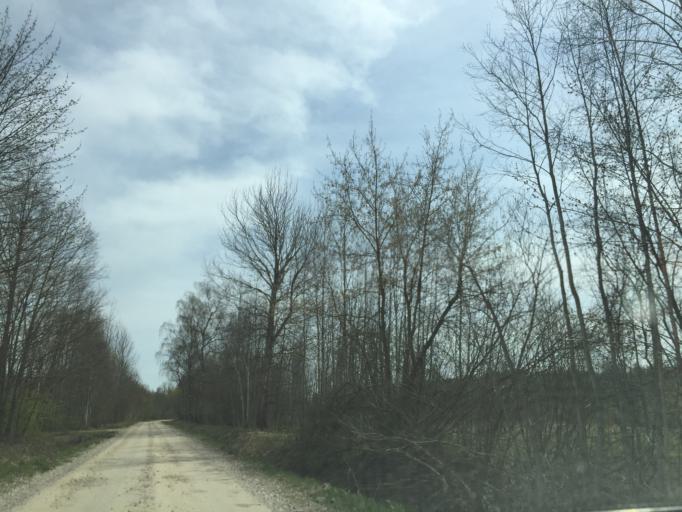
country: LV
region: Ludzas Rajons
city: Ludza
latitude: 56.5338
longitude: 27.5355
